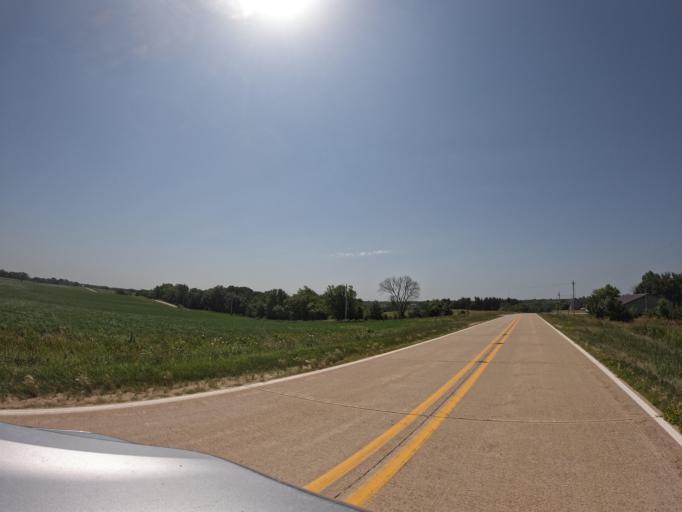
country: US
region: Iowa
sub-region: Henry County
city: Mount Pleasant
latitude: 40.8689
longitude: -91.5601
